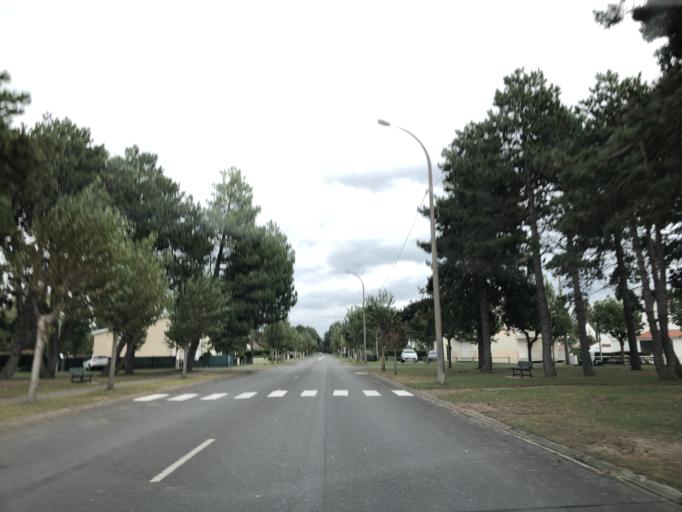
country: FR
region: Nord-Pas-de-Calais
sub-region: Departement du Pas-de-Calais
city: Cucq
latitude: 50.4786
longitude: 1.5915
